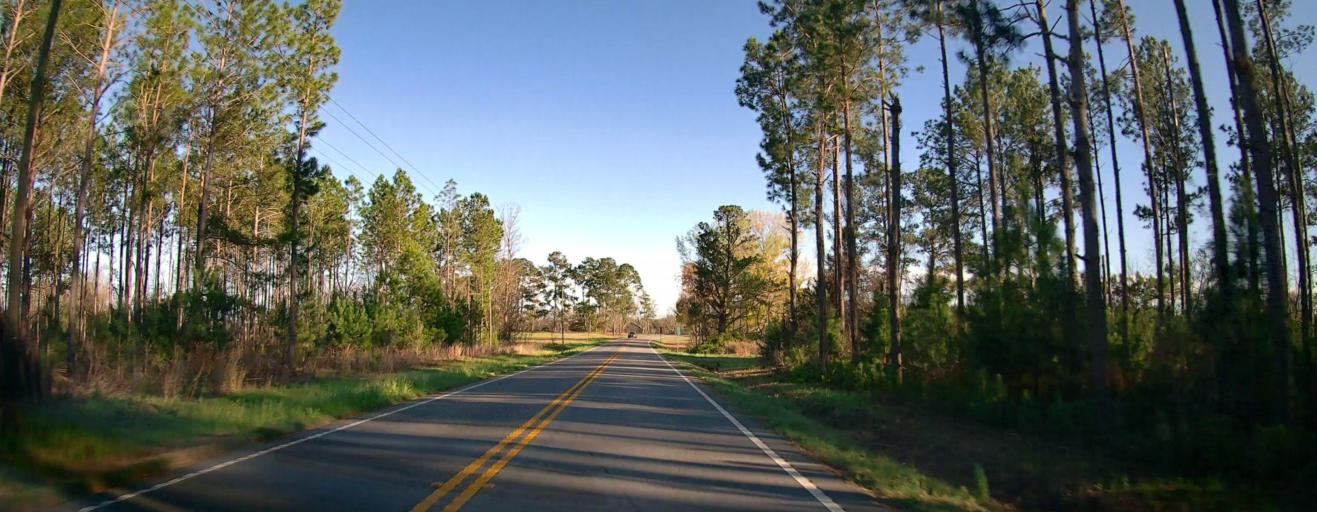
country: US
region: Georgia
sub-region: Pulaski County
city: Hawkinsville
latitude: 32.2084
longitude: -83.3783
